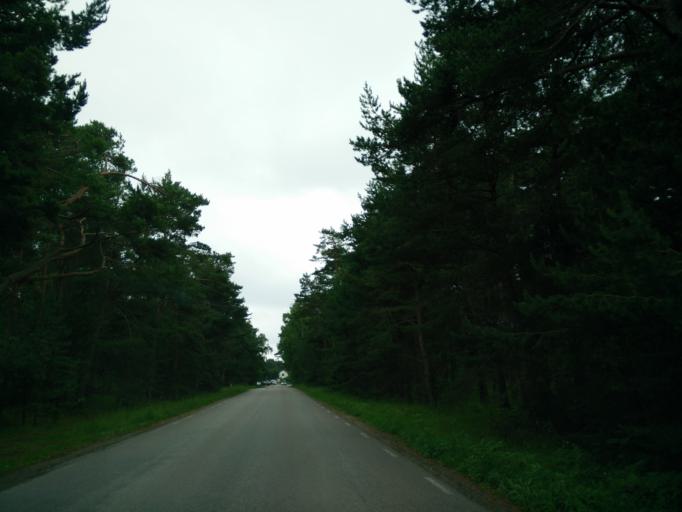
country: SE
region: Gotland
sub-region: Gotland
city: Slite
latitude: 57.9636
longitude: 19.2374
